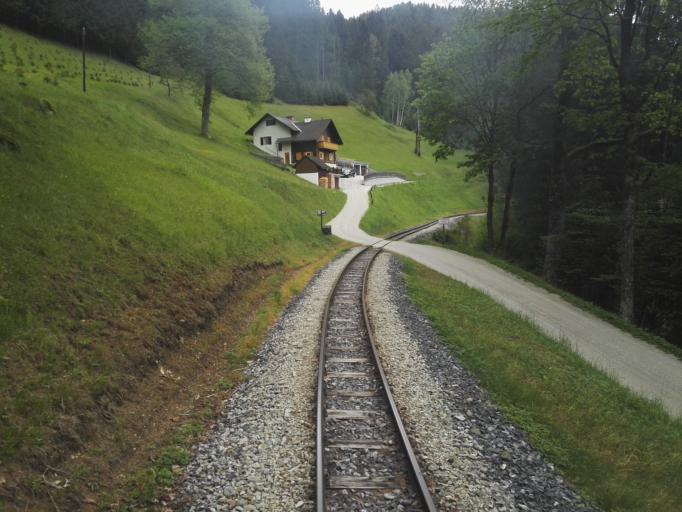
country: AT
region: Styria
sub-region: Politischer Bezirk Weiz
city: Birkfeld
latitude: 47.3409
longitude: 15.7014
